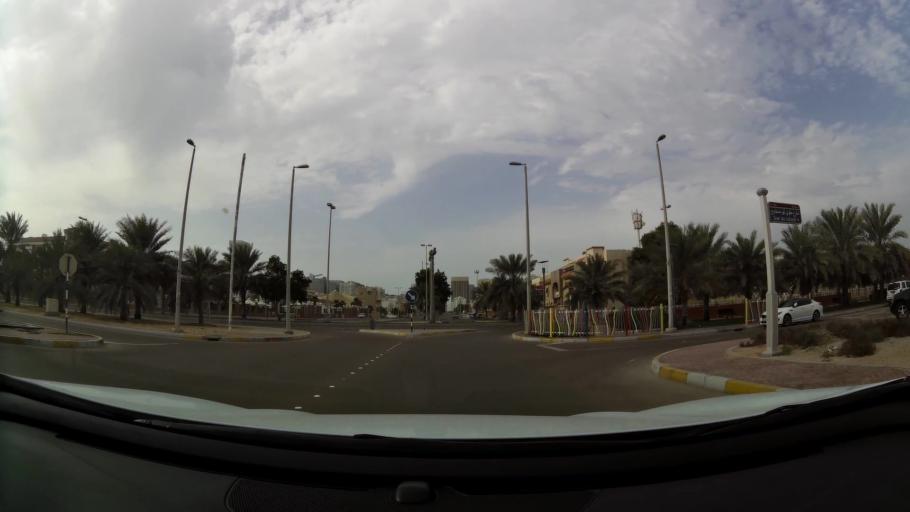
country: AE
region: Abu Dhabi
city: Abu Dhabi
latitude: 24.4641
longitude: 54.3516
